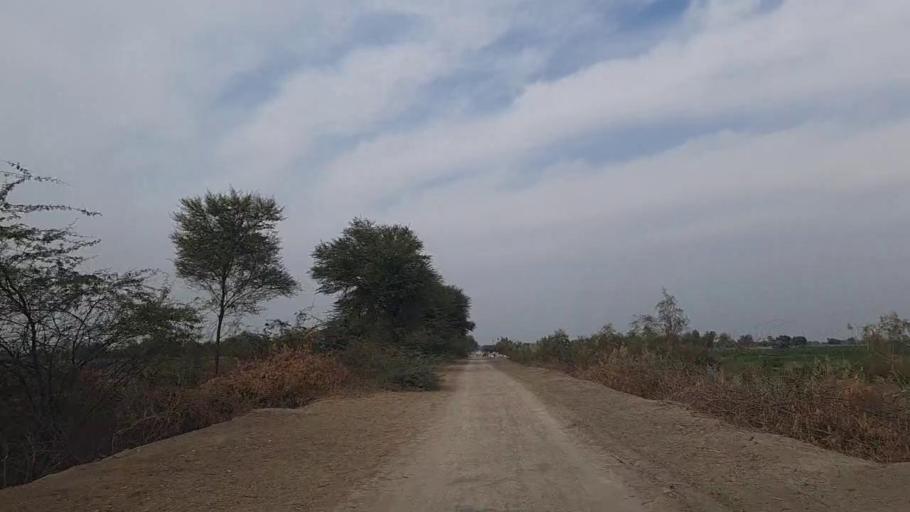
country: PK
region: Sindh
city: Daur
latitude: 26.4346
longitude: 68.4641
